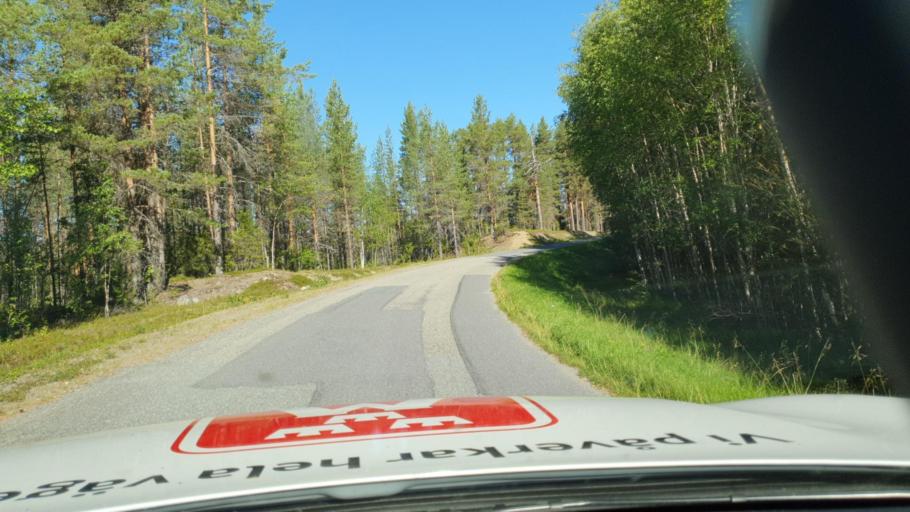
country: SE
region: Vaesterbotten
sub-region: Dorotea Kommun
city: Dorotea
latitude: 64.1642
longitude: 16.2582
